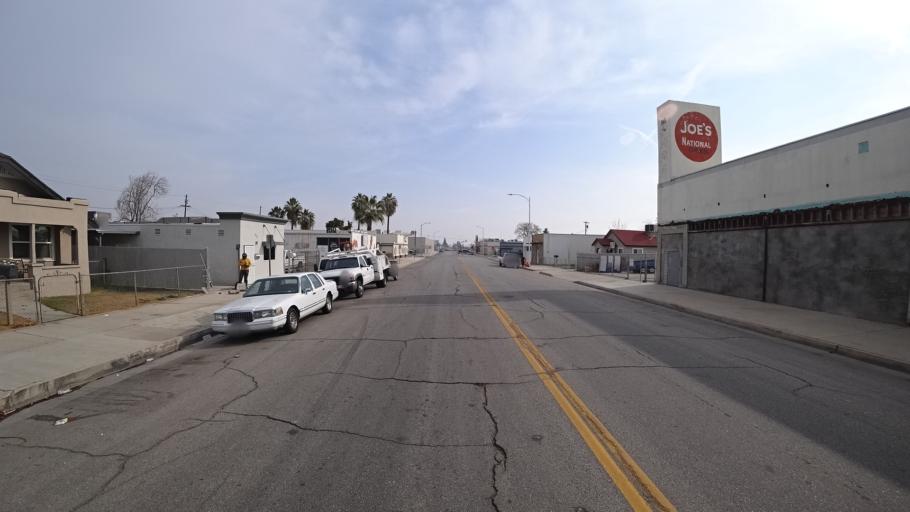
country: US
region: California
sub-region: Kern County
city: Bakersfield
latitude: 35.3744
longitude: -118.9966
